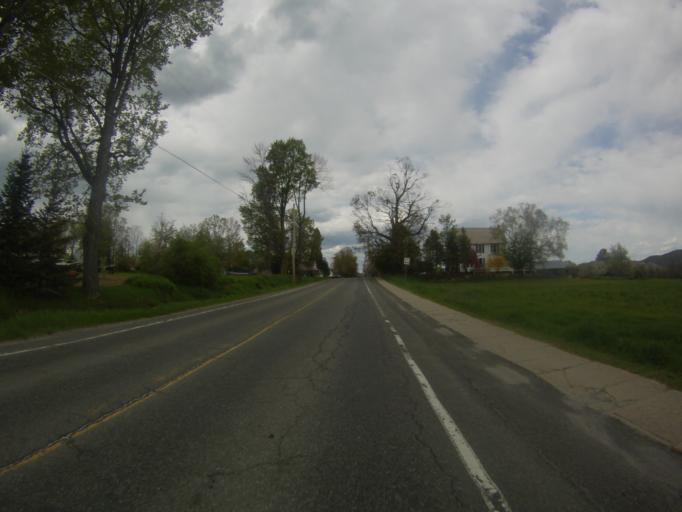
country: US
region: New York
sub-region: Essex County
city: Mineville
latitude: 44.0502
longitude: -73.5069
